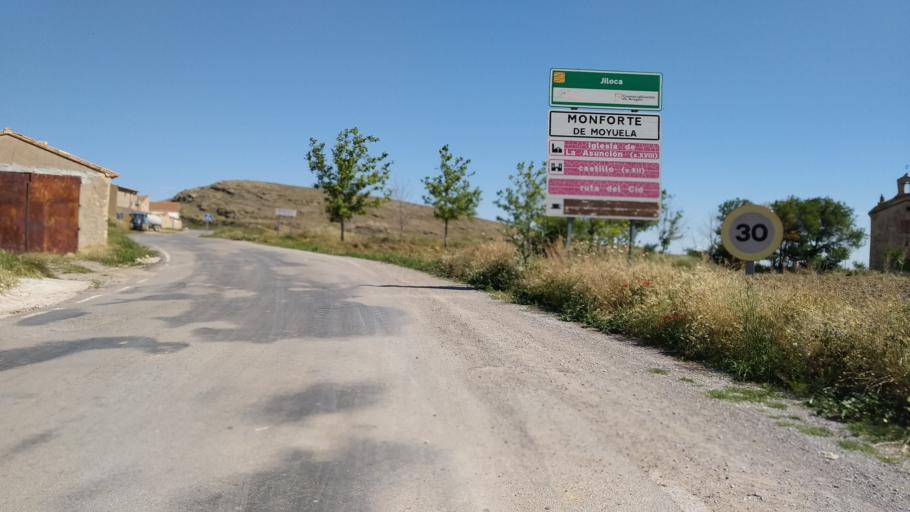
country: ES
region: Aragon
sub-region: Provincia de Teruel
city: Monforte de Moyuela
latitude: 41.0543
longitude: -1.0126
